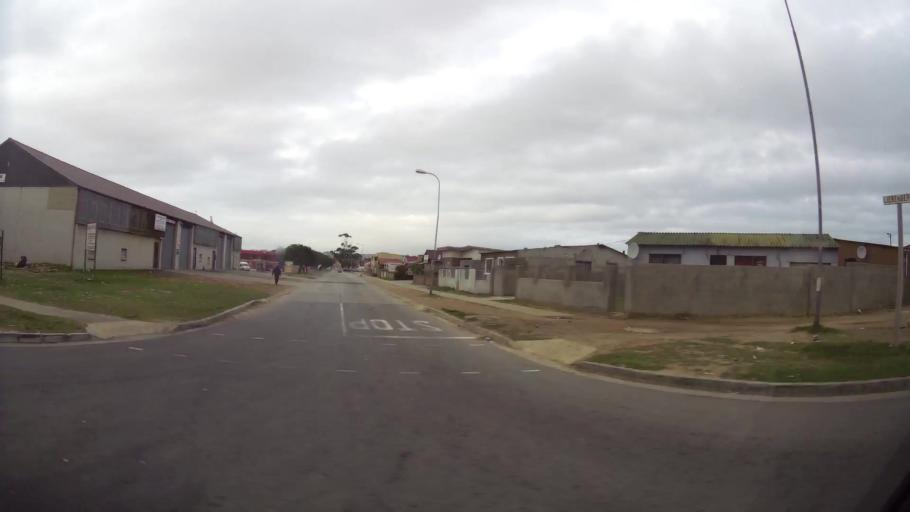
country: ZA
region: Eastern Cape
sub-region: Nelson Mandela Bay Metropolitan Municipality
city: Port Elizabeth
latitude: -33.9108
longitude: 25.5567
